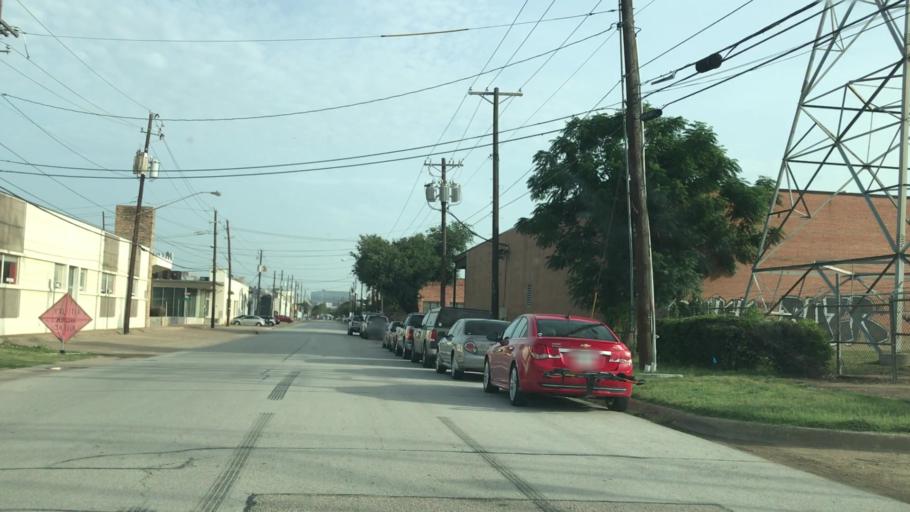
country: US
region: Texas
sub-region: Dallas County
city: Dallas
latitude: 32.7860
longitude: -96.8158
